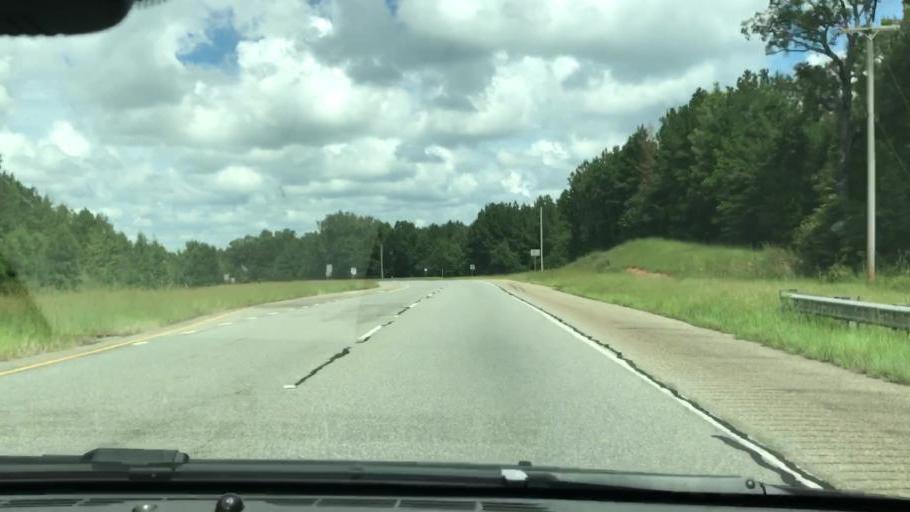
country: US
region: Georgia
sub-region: Stewart County
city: Lumpkin
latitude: 32.1161
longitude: -84.8141
